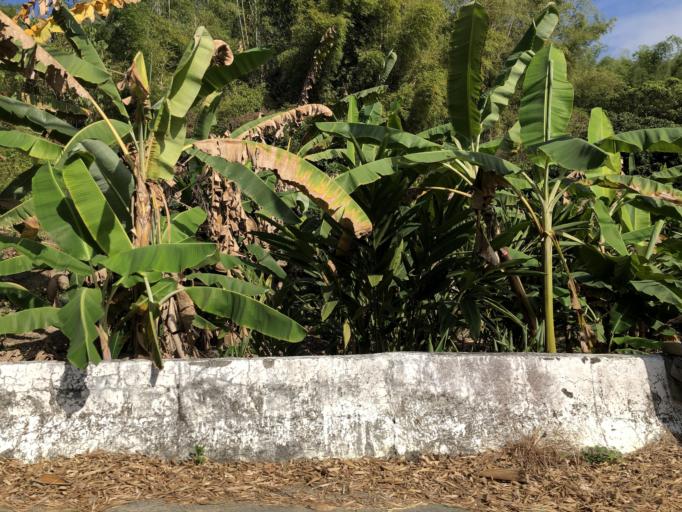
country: TW
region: Taiwan
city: Yujing
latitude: 23.0208
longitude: 120.3976
